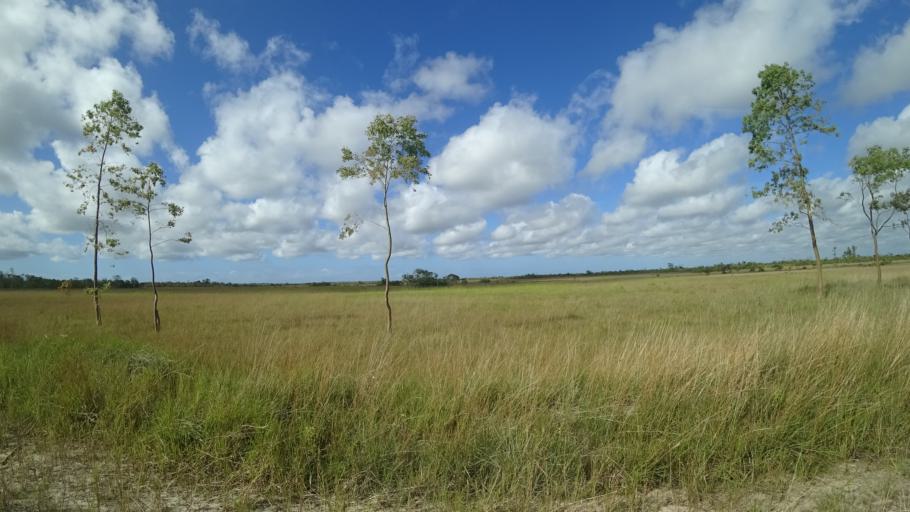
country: MZ
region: Sofala
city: Beira
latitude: -19.6126
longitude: 35.0723
